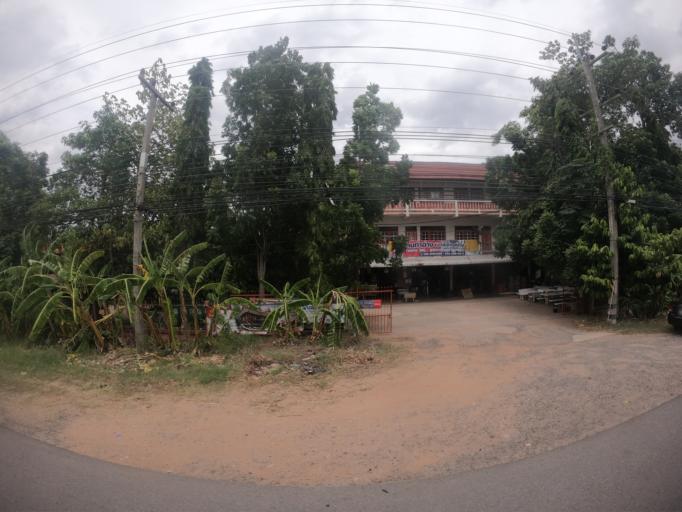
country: TH
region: Nakhon Ratchasima
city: Chok Chai
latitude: 14.8340
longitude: 102.1846
